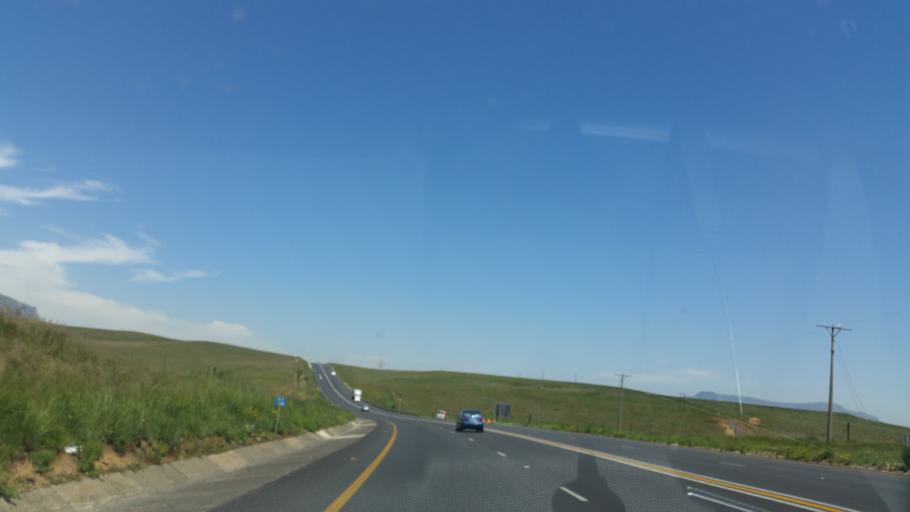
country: ZA
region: Orange Free State
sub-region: Thabo Mofutsanyana District Municipality
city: Harrismith
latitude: -28.3666
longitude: 29.3563
